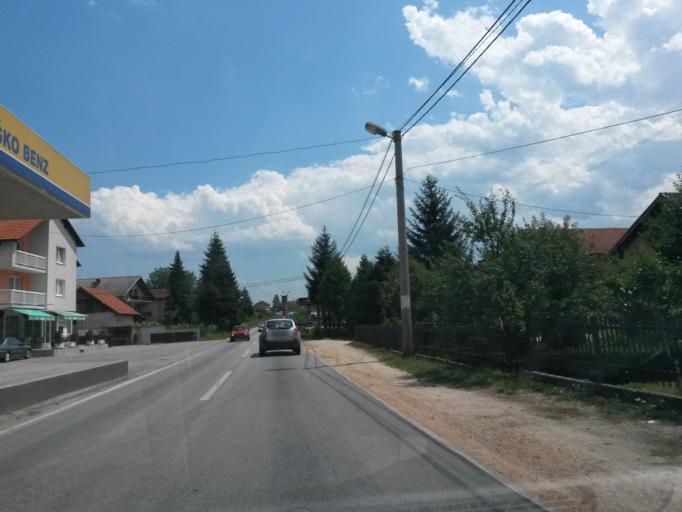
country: BA
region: Federation of Bosnia and Herzegovina
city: Vitez
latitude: 44.1857
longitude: 17.7451
